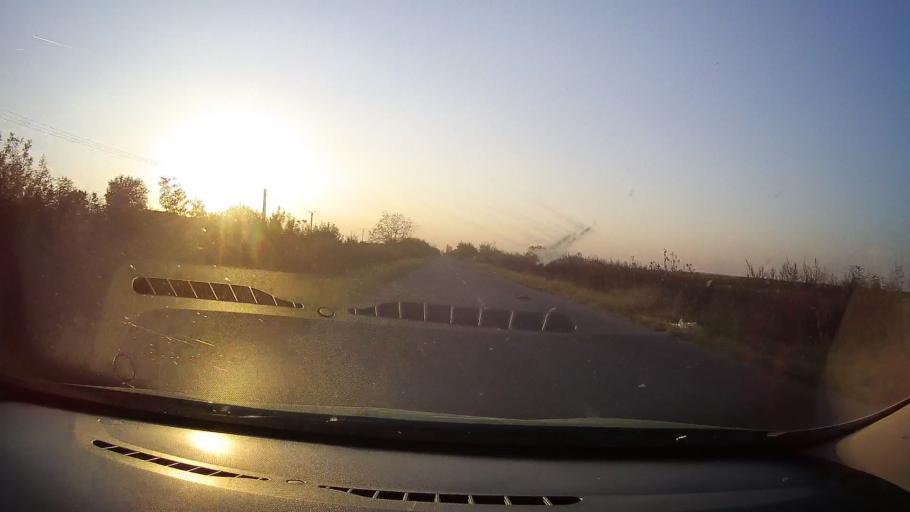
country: RO
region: Arad
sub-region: Comuna Ineu
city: Ineu
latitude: 46.4304
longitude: 21.8189
